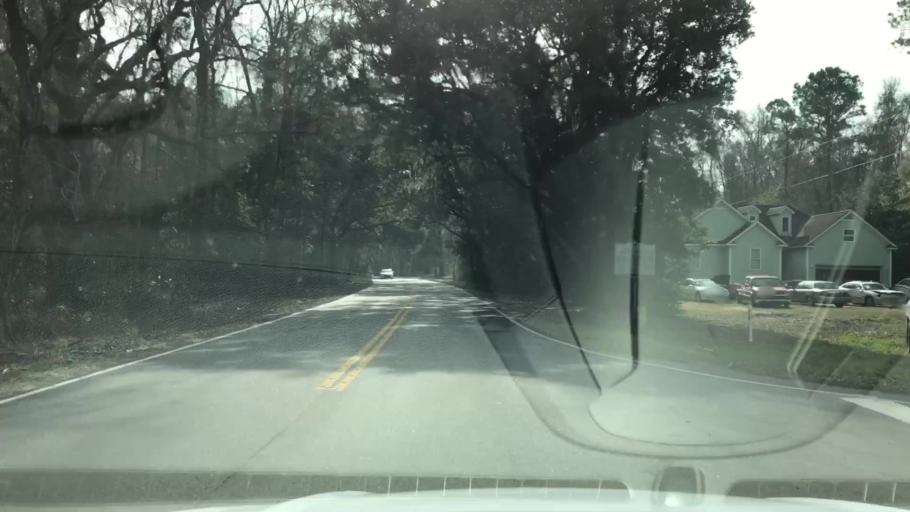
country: US
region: South Carolina
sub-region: Charleston County
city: Folly Beach
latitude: 32.7186
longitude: -80.0215
